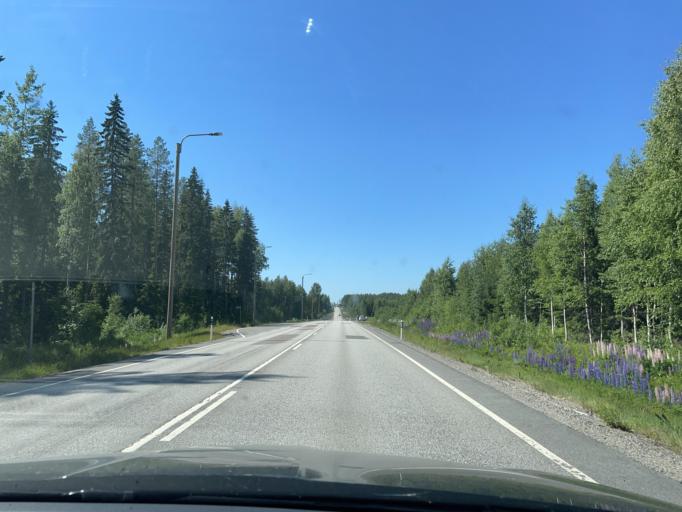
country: FI
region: Central Finland
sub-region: Saarijaervi-Viitasaari
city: Viitasaari
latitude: 63.1449
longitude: 25.8032
